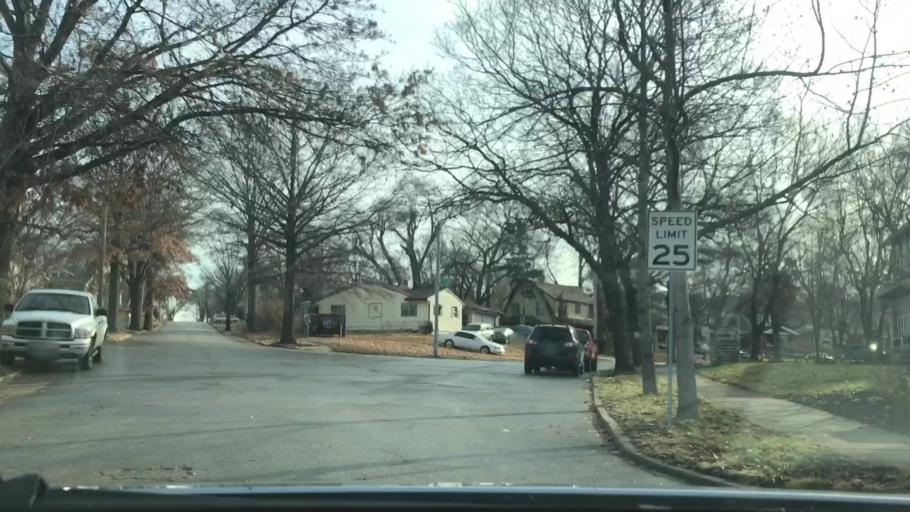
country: US
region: Kansas
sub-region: Johnson County
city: Westwood
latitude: 39.0323
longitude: -94.5641
